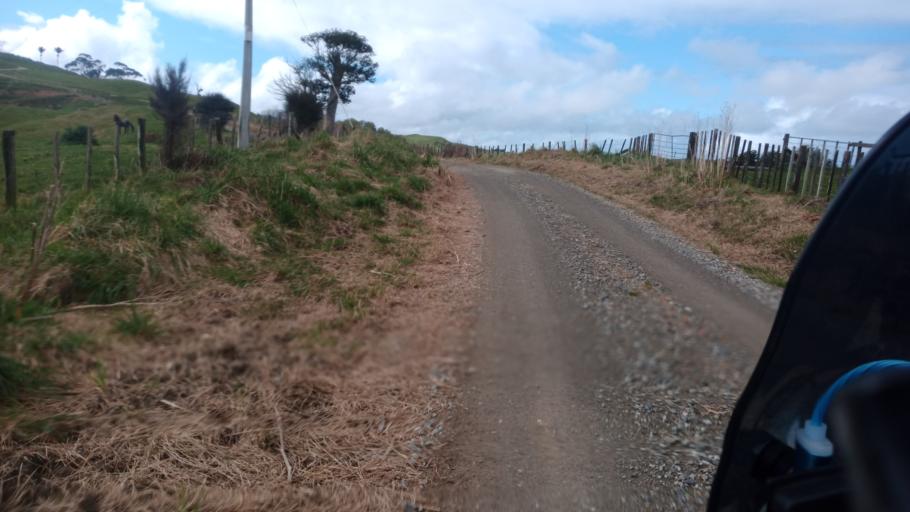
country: NZ
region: Gisborne
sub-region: Gisborne District
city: Gisborne
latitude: -38.4987
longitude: 178.2059
